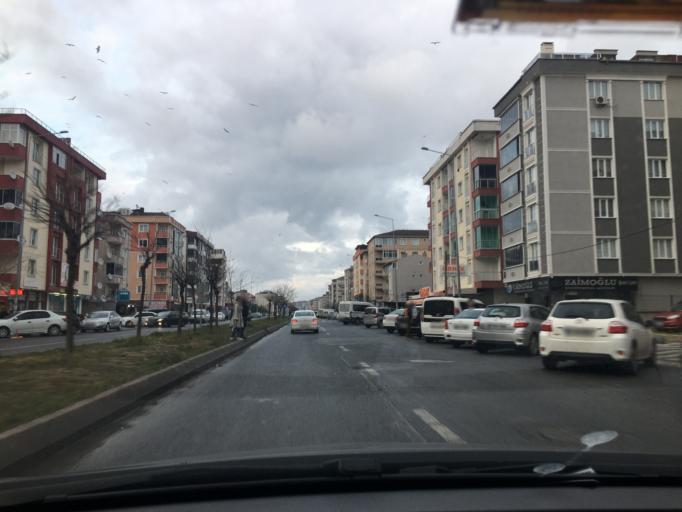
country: TR
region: Tekirdag
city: Cerkezkoey
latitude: 41.2822
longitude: 27.9837
